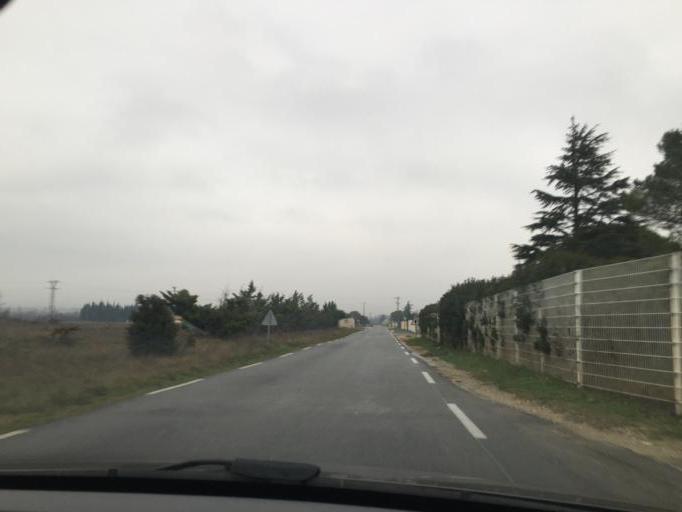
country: FR
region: Provence-Alpes-Cote d'Azur
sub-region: Departement du Vaucluse
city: Maubec
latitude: 43.8768
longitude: 5.1560
